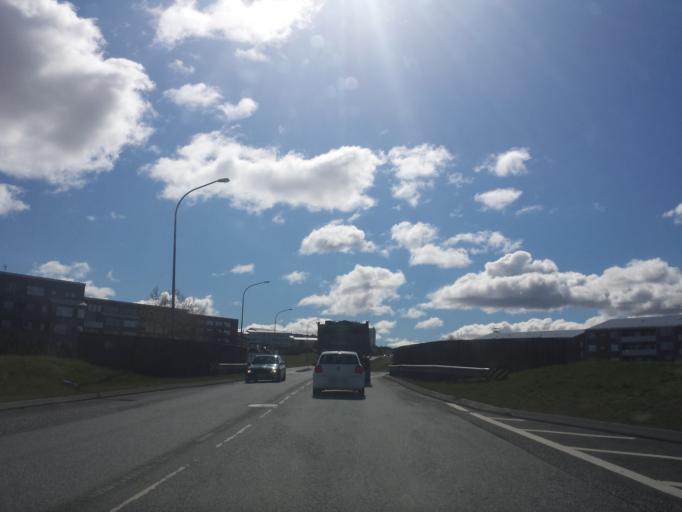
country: IS
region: Capital Region
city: Kopavogur
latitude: 64.0990
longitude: -21.8716
